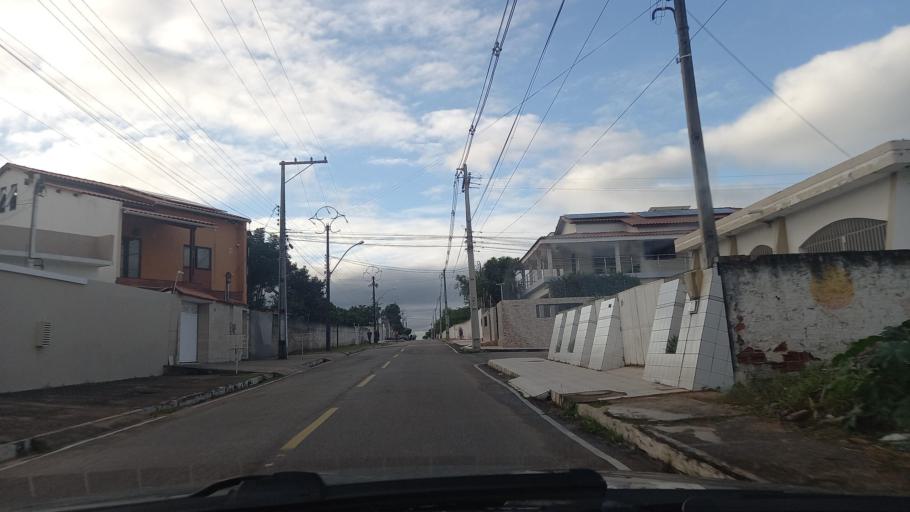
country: BR
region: Bahia
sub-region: Paulo Afonso
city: Paulo Afonso
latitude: -9.3926
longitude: -38.2319
